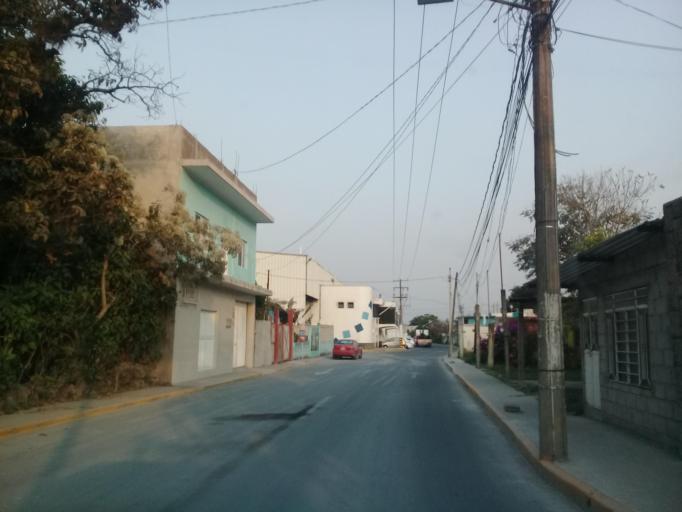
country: MX
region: Veracruz
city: Ixtac Zoquitlan
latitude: 18.8524
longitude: -97.0561
